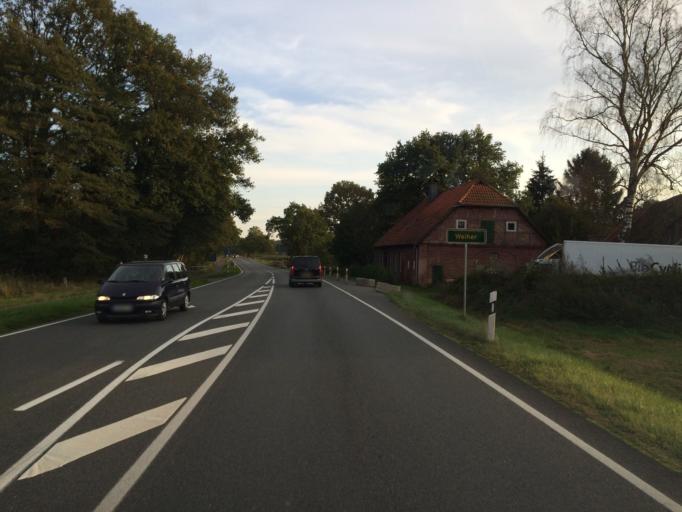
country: DE
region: Lower Saxony
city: Soltau
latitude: 52.9684
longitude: 9.8528
